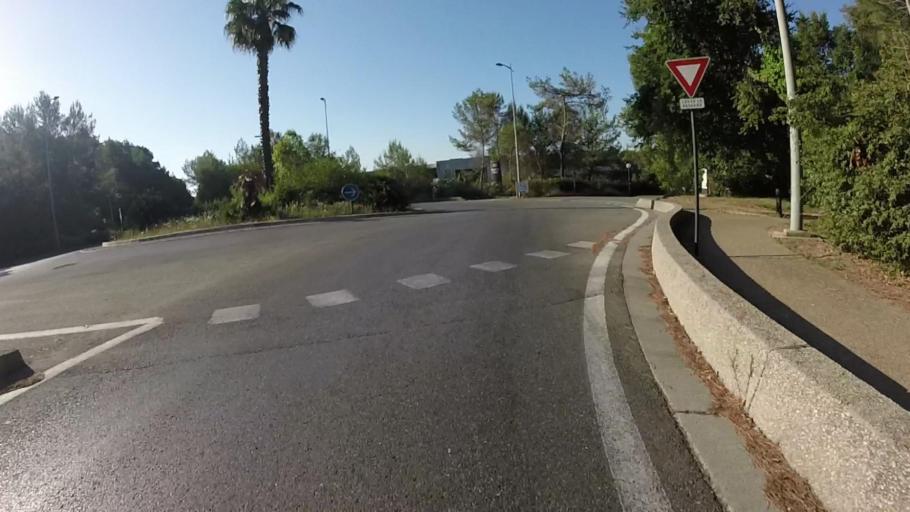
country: FR
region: Provence-Alpes-Cote d'Azur
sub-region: Departement des Alpes-Maritimes
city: Mougins
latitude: 43.6114
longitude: 7.0171
